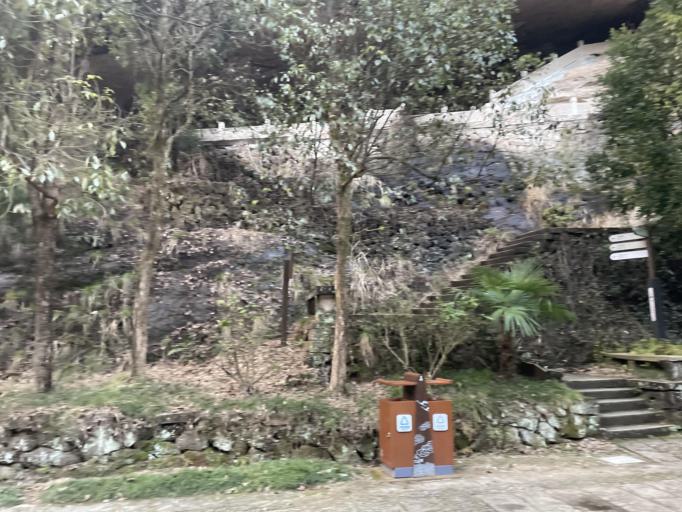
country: CN
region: Zhejiang Sheng
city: Shuhong
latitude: 28.6897
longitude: 120.1271
